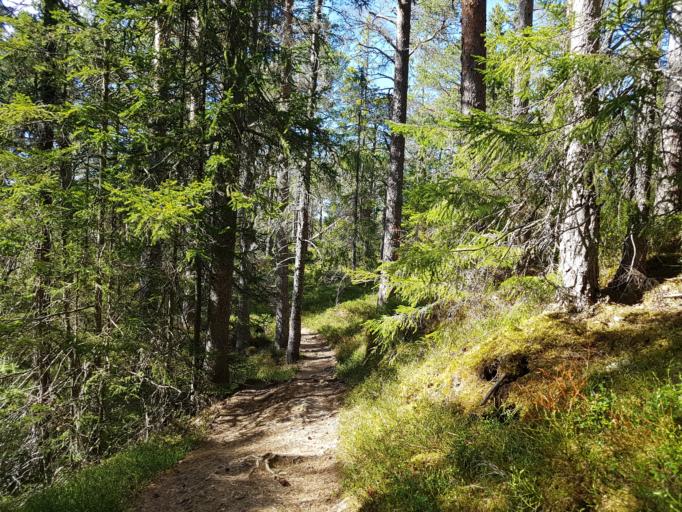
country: NO
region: Sor-Trondelag
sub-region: Trondheim
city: Trondheim
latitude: 63.4437
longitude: 10.3077
